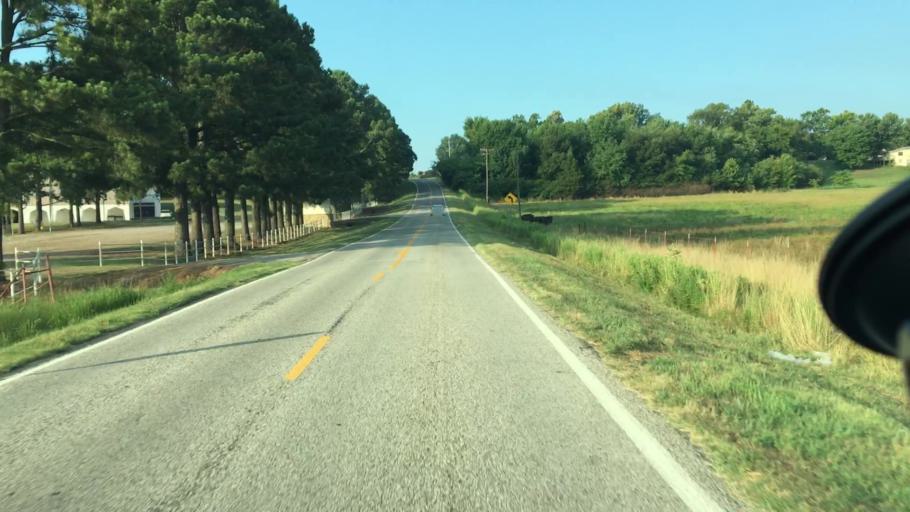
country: US
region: Arkansas
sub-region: Logan County
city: Paris
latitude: 35.3023
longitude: -93.6347
